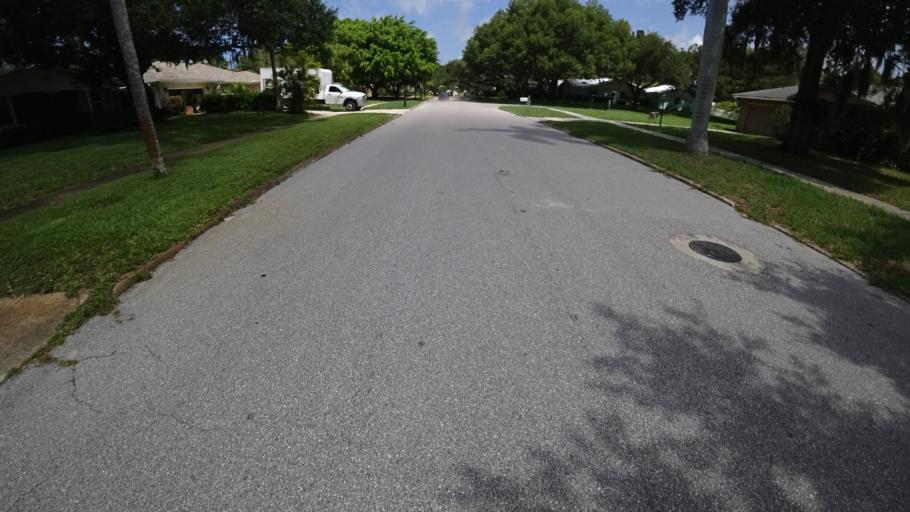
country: US
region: Florida
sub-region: Manatee County
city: Whitfield
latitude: 27.4102
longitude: -82.5753
